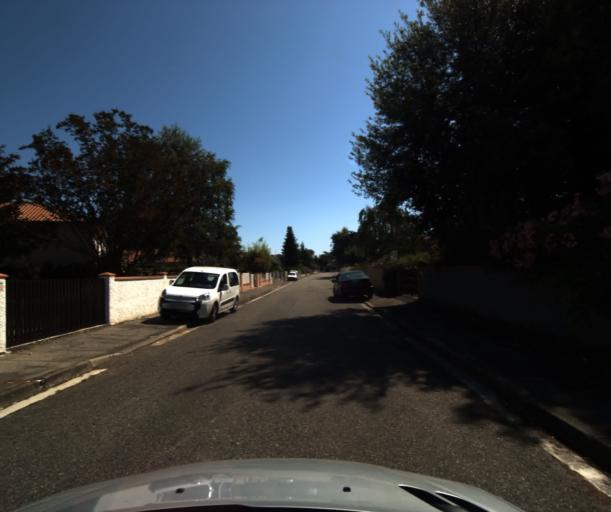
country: FR
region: Midi-Pyrenees
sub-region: Departement de la Haute-Garonne
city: Roquettes
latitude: 43.5017
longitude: 1.3668
